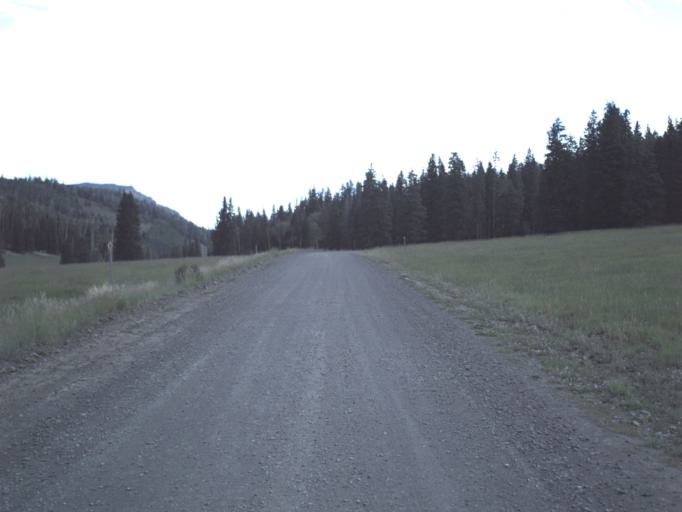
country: US
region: Utah
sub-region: Piute County
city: Junction
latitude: 38.2372
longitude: -112.3599
